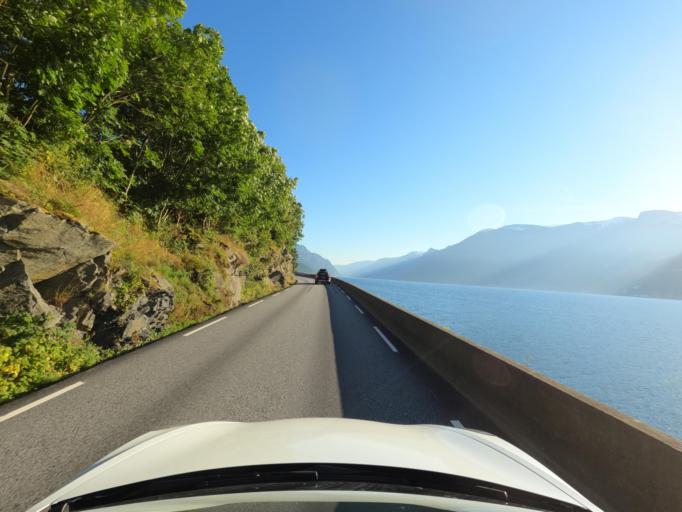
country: NO
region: Hordaland
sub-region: Ullensvang
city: Kinsarvik
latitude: 60.2747
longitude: 6.6183
